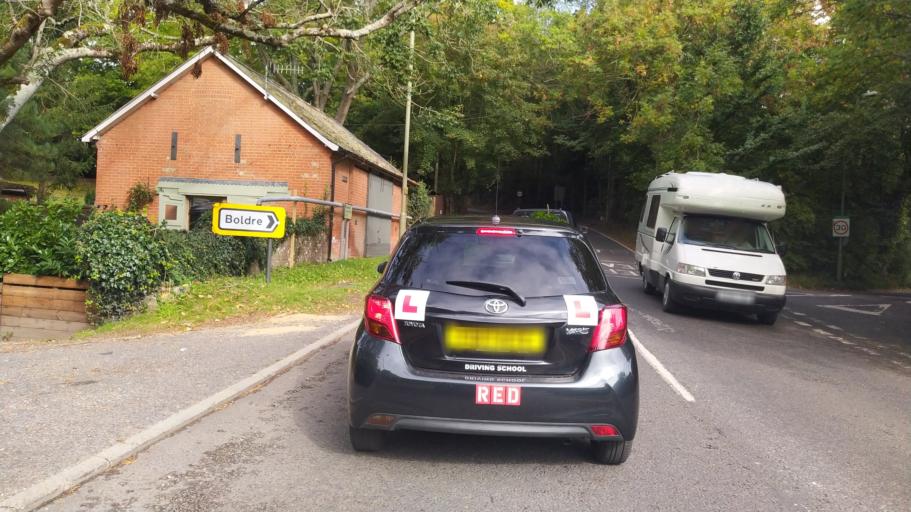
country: GB
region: England
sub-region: Hampshire
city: Lymington
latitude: 50.7724
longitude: -1.5520
